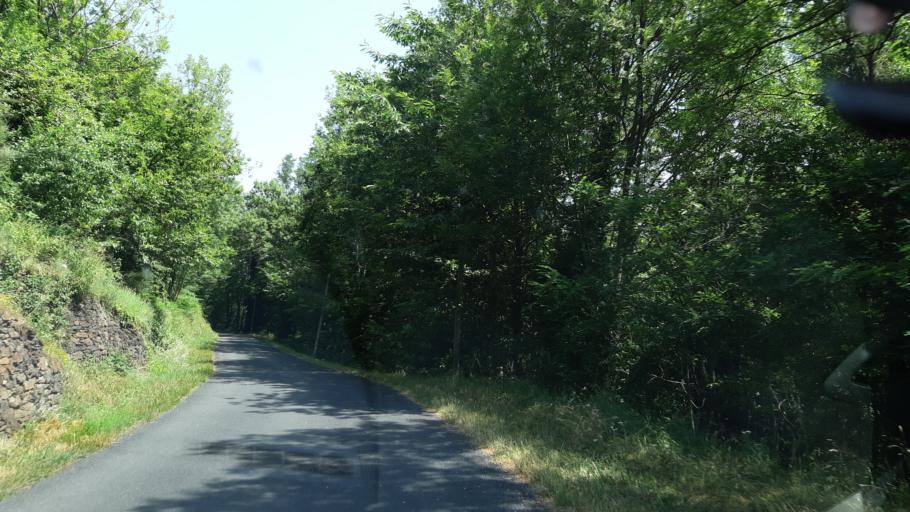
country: FR
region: Languedoc-Roussillon
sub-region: Departement des Pyrenees-Orientales
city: Arles
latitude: 42.5430
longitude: 2.5878
